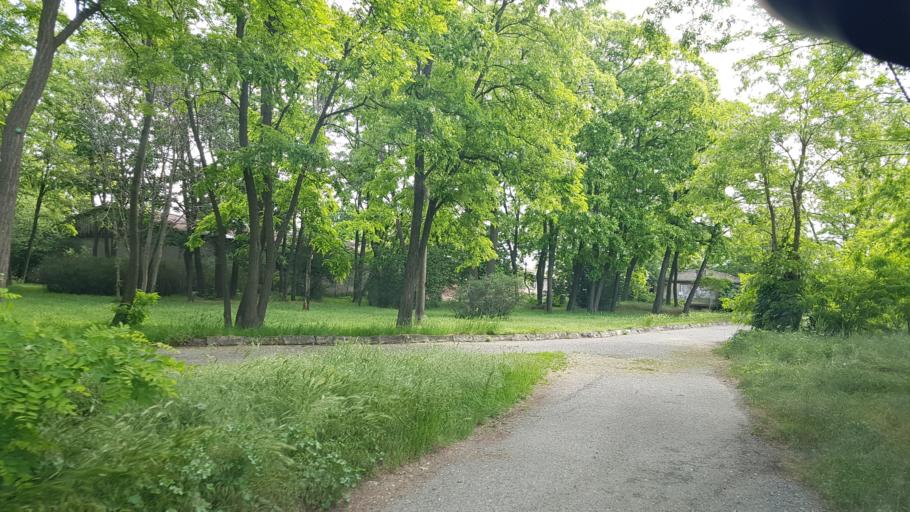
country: DE
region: Brandenburg
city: Crinitz
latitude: 51.8047
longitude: 13.8189
